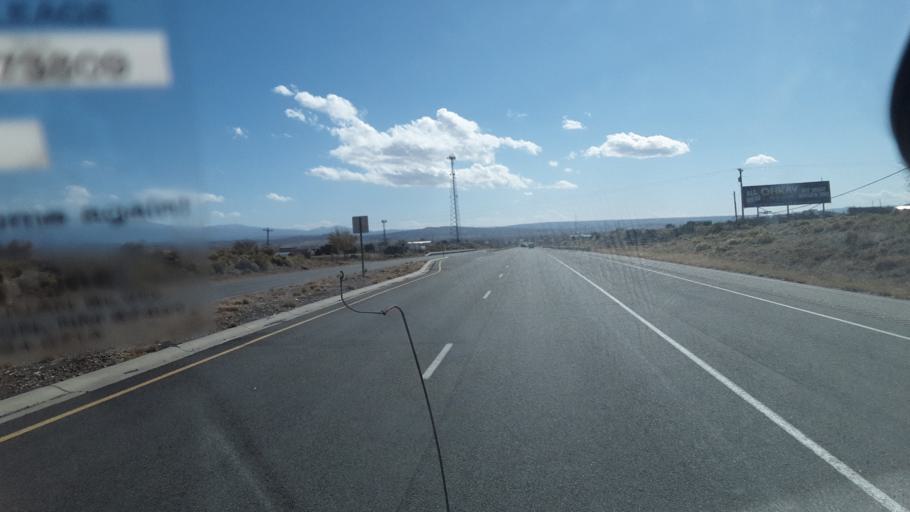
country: US
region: New Mexico
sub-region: Rio Arriba County
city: Espanola
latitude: 36.0185
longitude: -106.0906
